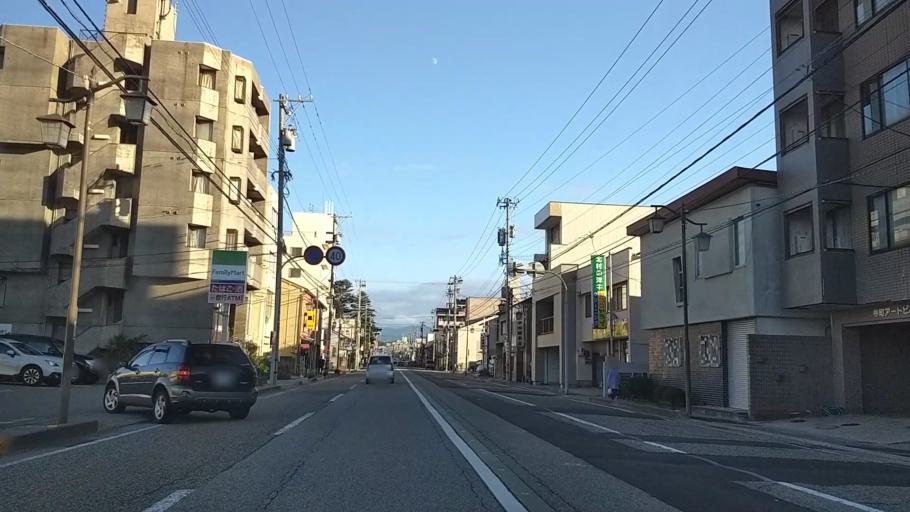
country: JP
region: Ishikawa
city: Nonoichi
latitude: 36.5489
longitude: 136.6569
